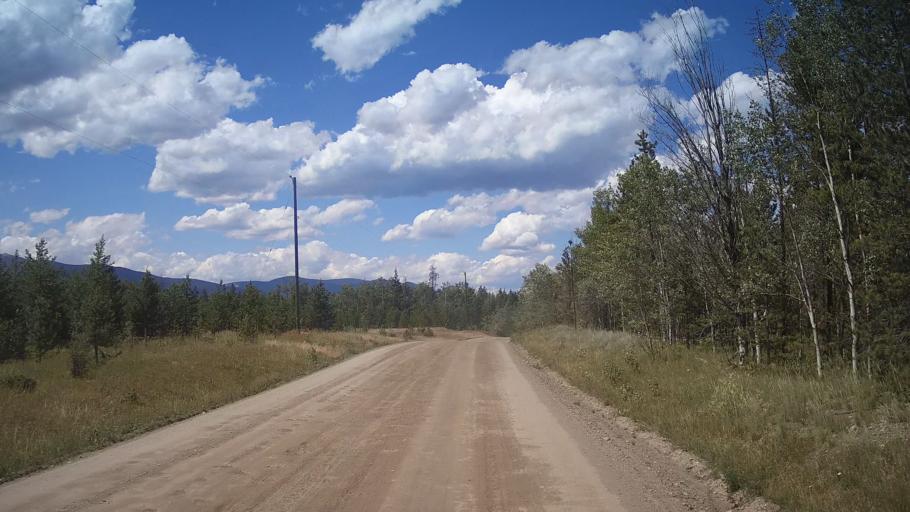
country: CA
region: British Columbia
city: Cache Creek
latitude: 51.2679
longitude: -121.7060
